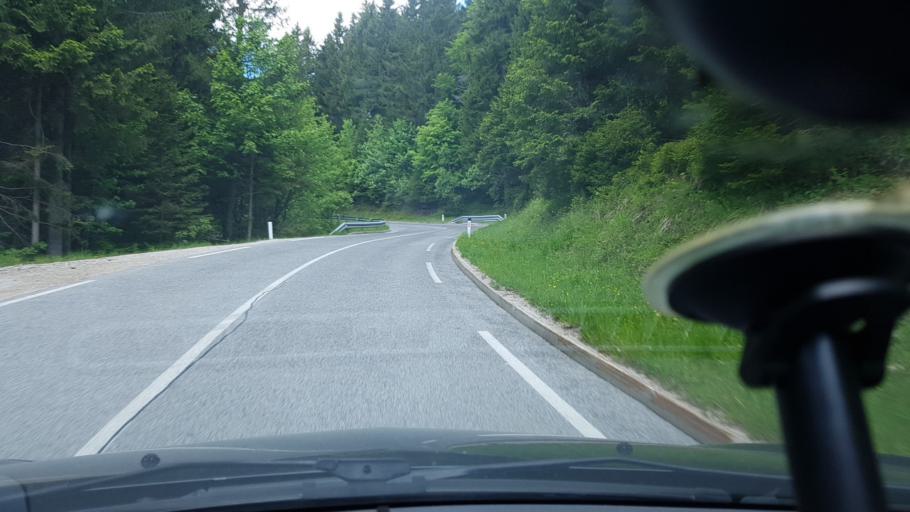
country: SI
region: Zrece
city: Zrece
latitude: 46.4463
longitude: 15.3478
